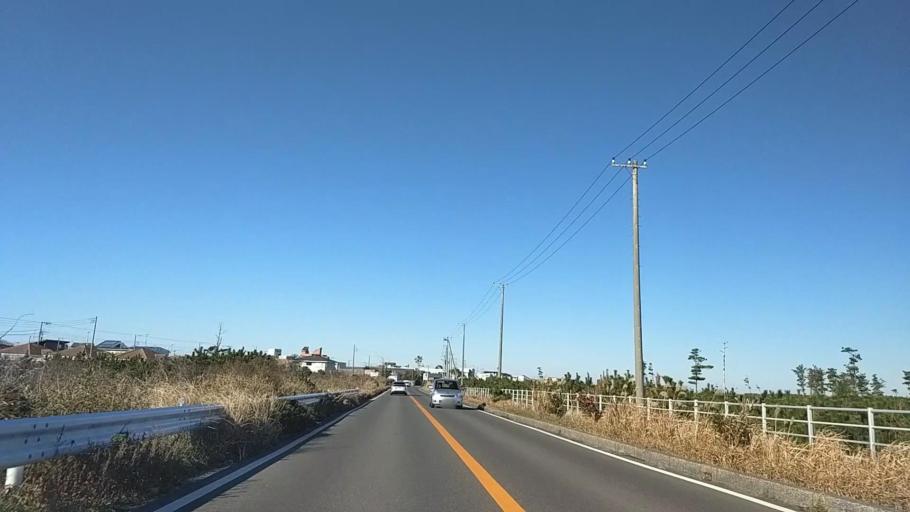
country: JP
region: Chiba
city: Ohara
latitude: 35.3499
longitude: 140.3903
